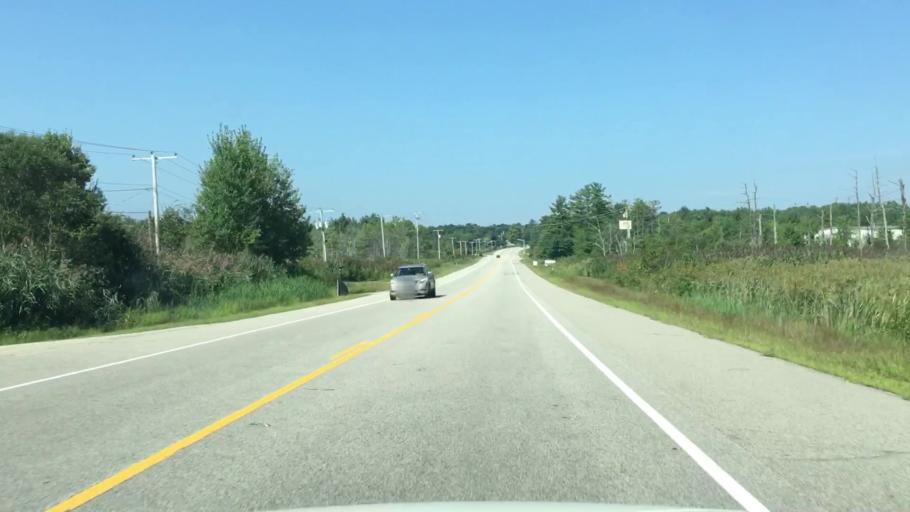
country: US
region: New Hampshire
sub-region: Rockingham County
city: Seabrook
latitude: 42.8976
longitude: -70.8936
